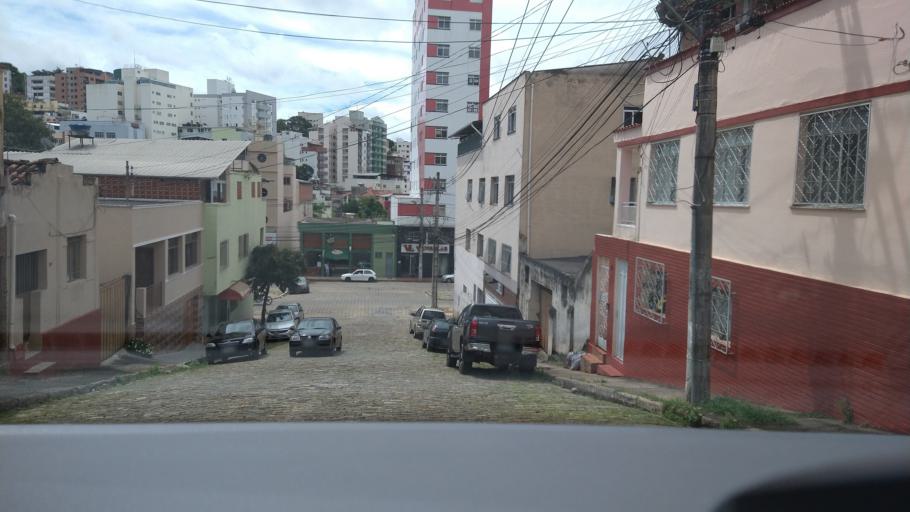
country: BR
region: Minas Gerais
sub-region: Vicosa
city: Vicosa
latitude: -20.7584
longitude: -42.8784
